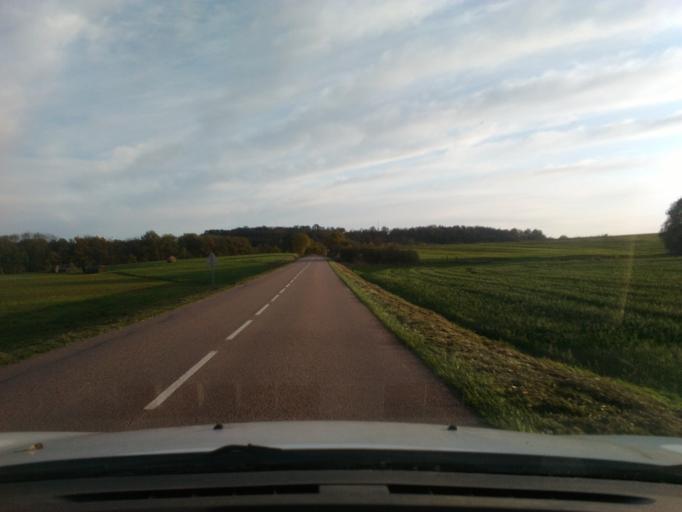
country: FR
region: Lorraine
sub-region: Departement des Vosges
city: Mirecourt
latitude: 48.2214
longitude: 6.1554
